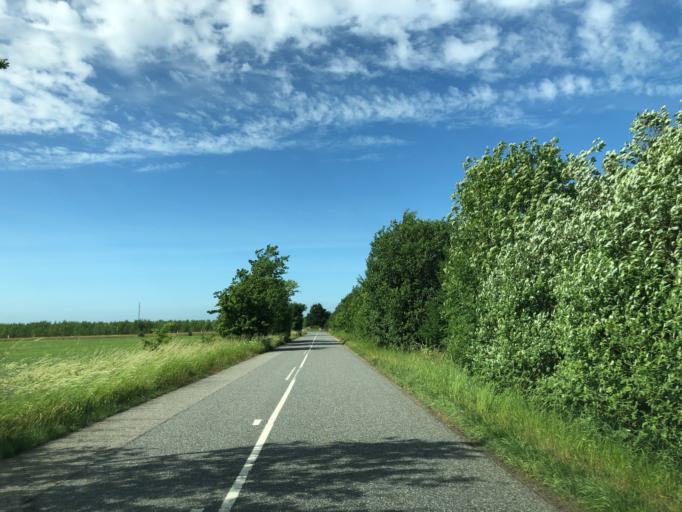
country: DK
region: Central Jutland
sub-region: Herning Kommune
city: Snejbjerg
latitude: 56.0755
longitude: 8.9143
